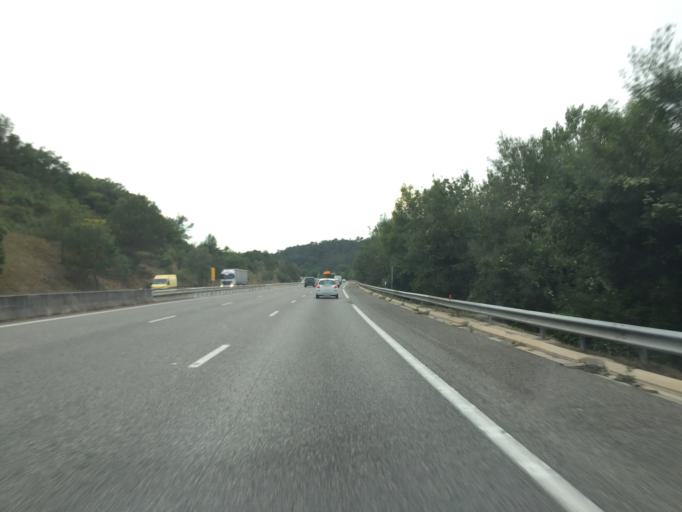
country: FR
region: Provence-Alpes-Cote d'Azur
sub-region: Departement du Var
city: Camps-la-Source
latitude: 43.4181
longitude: 6.1052
